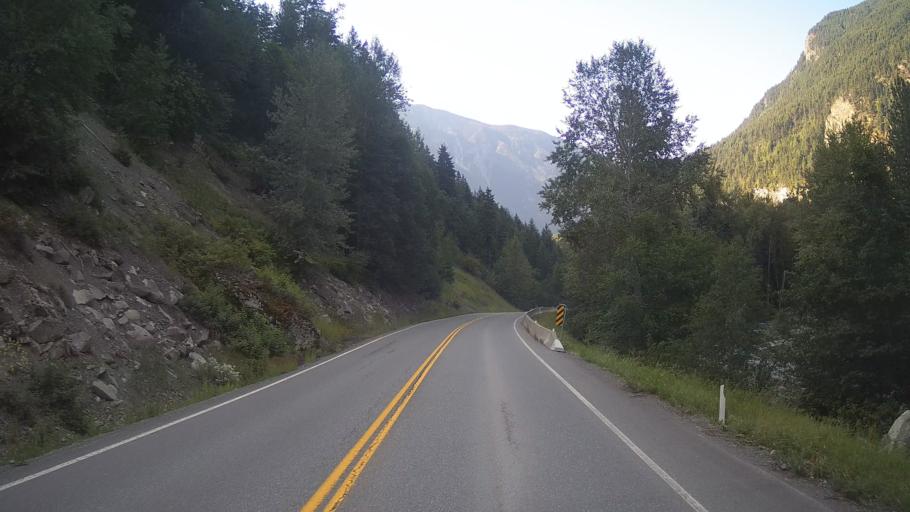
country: CA
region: British Columbia
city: Lillooet
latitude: 50.5938
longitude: -122.0937
